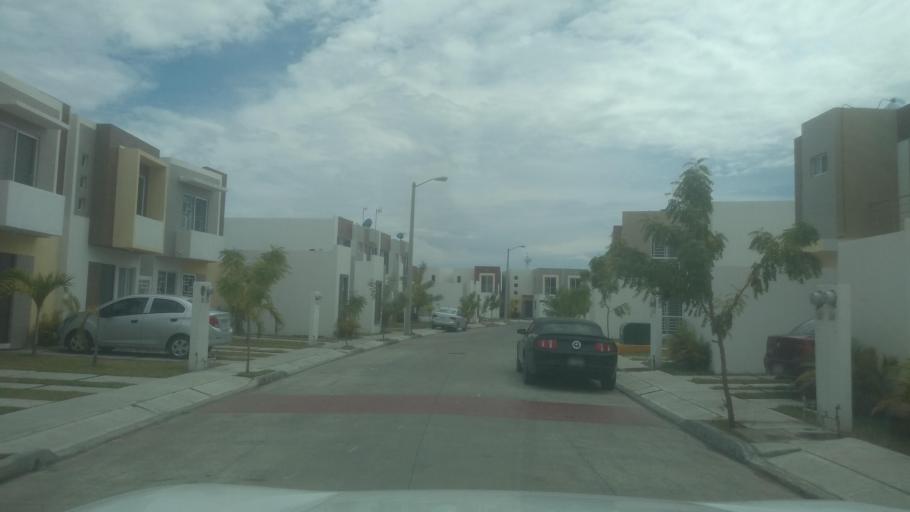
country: MX
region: Veracruz
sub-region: Medellin
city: Fraccionamiento Arboledas San Ramon
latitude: 19.1053
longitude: -96.1641
